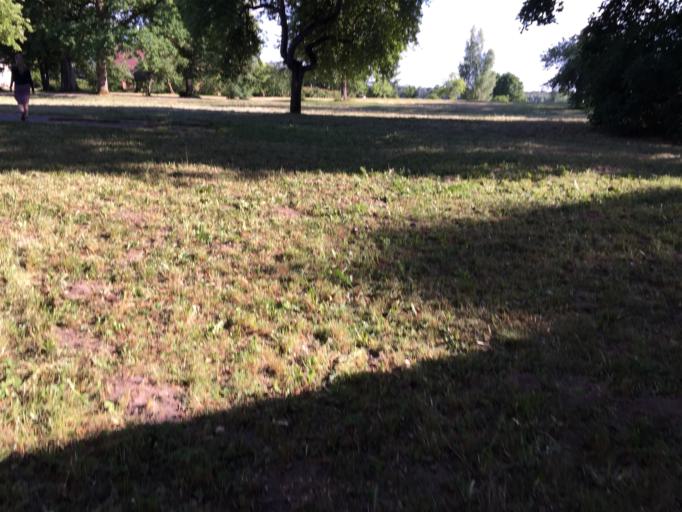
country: LV
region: Aizkraukles Rajons
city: Aizkraukle
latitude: 56.7912
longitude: 25.2672
